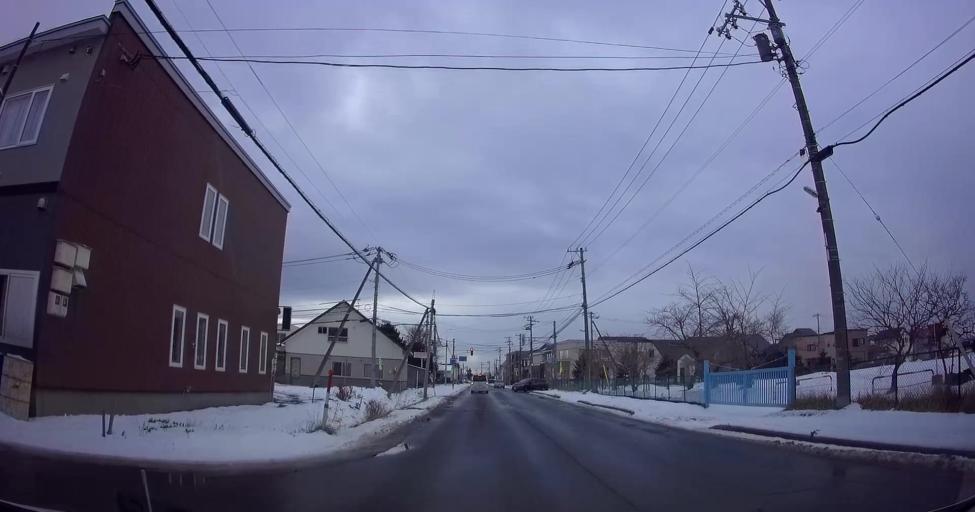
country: JP
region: Hokkaido
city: Kamiiso
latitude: 41.8289
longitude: 140.6870
